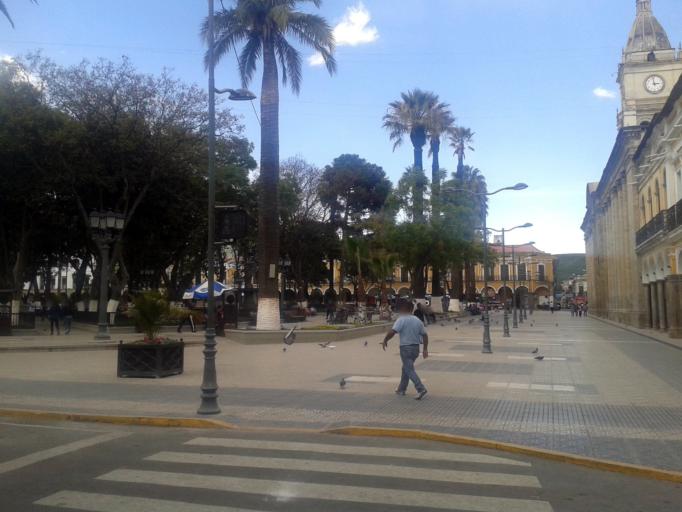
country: BO
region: Cochabamba
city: Cochabamba
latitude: -17.3943
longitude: -66.1574
